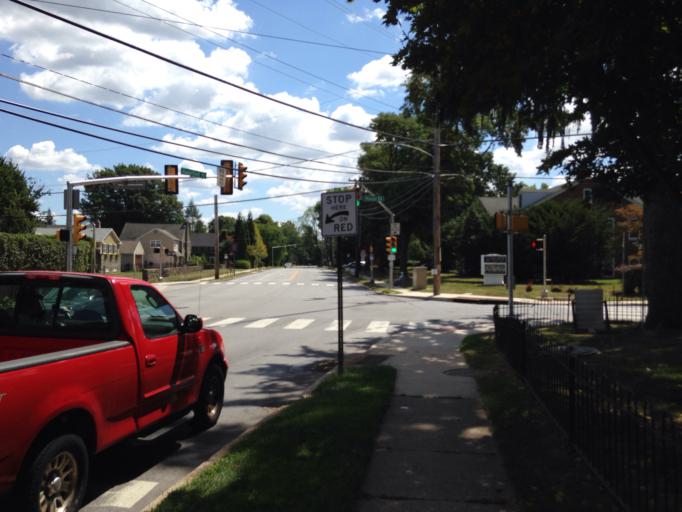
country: US
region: Pennsylvania
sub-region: Montgomery County
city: Penn Wynne
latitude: 39.9850
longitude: -75.2750
